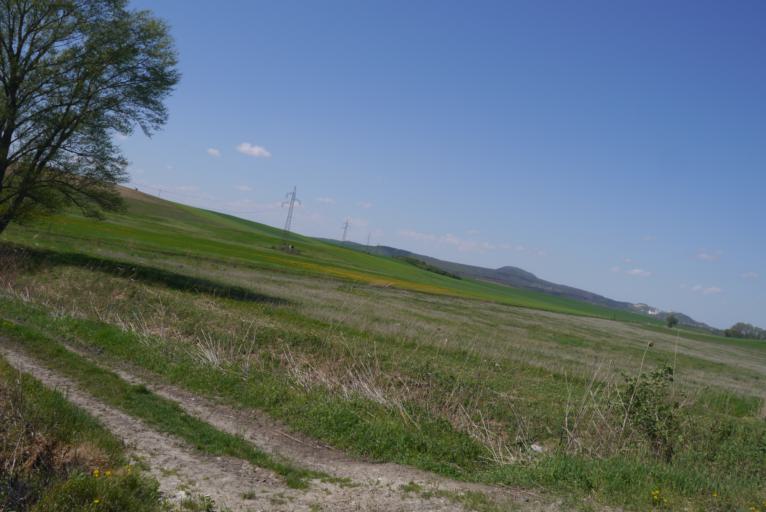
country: HU
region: Komarom-Esztergom
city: Kesztolc
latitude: 47.6921
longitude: 18.8008
